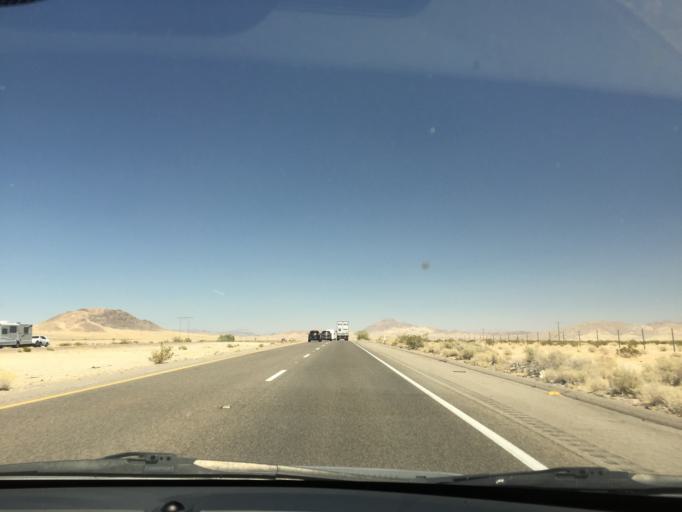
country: US
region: California
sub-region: San Bernardino County
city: Fort Irwin
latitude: 35.0177
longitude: -116.5121
